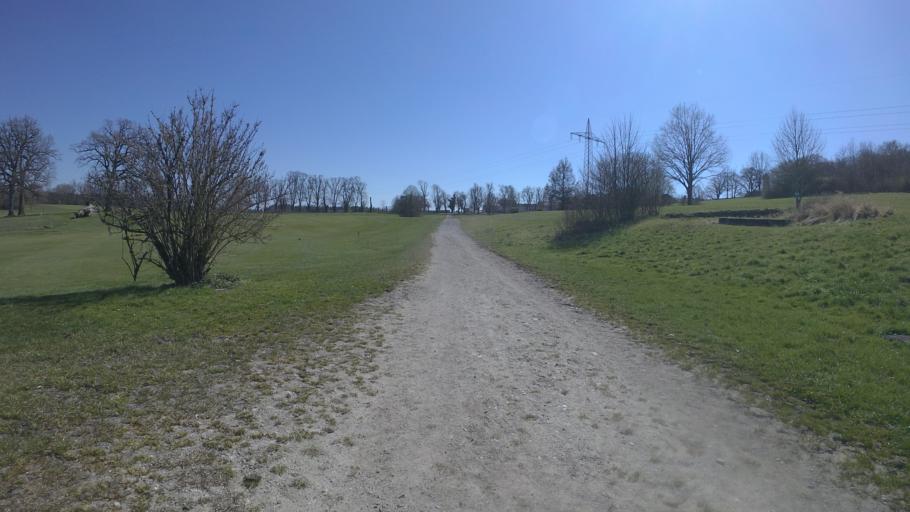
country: DE
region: Bavaria
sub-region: Upper Bavaria
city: Chieming
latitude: 47.9265
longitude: 12.5086
